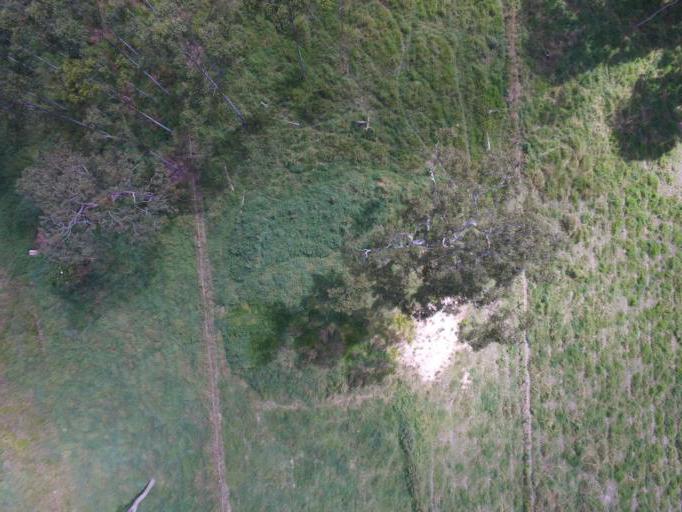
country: AU
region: Queensland
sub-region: Tablelands
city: Atherton
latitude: -17.3020
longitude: 145.4560
